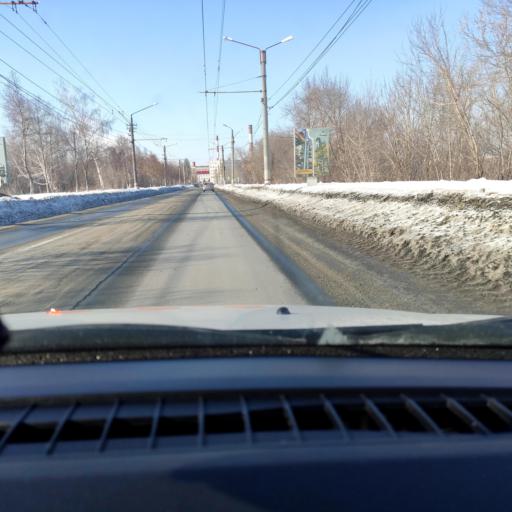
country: RU
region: Samara
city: Novokuybyshevsk
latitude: 53.1051
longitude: 49.9327
